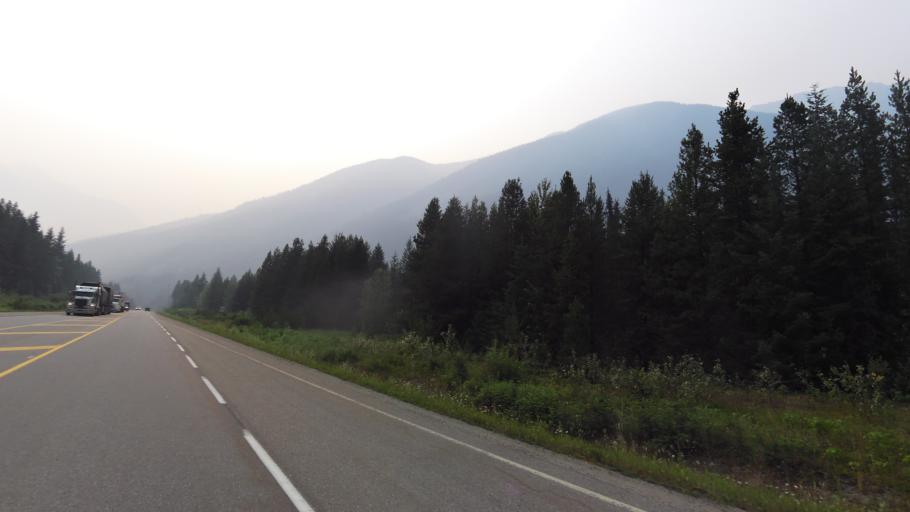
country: CA
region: Alberta
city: Grande Cache
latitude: 53.0327
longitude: -119.2429
